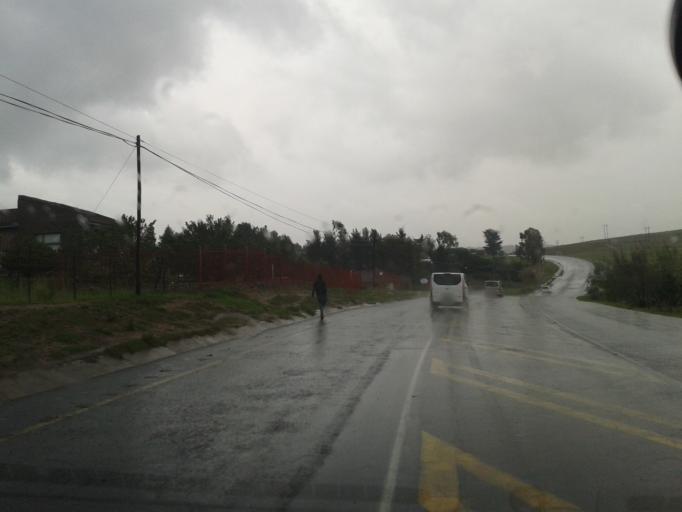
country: LS
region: Maseru
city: Nako
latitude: -29.6290
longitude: 27.4858
